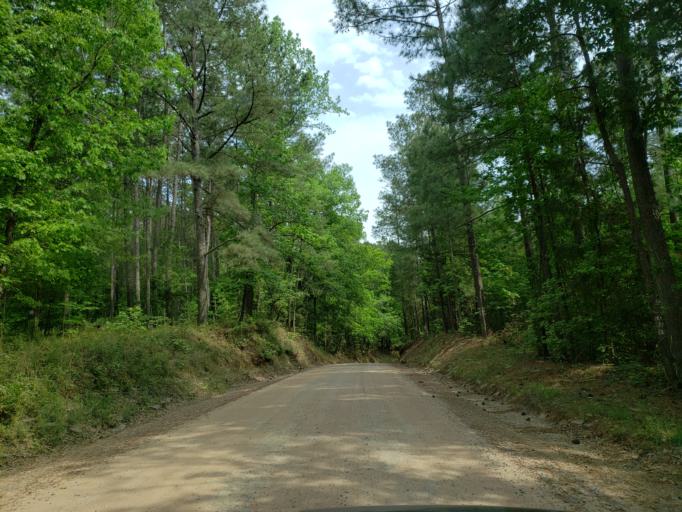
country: US
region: Georgia
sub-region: Monroe County
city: Forsyth
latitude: 32.9864
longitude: -83.9157
